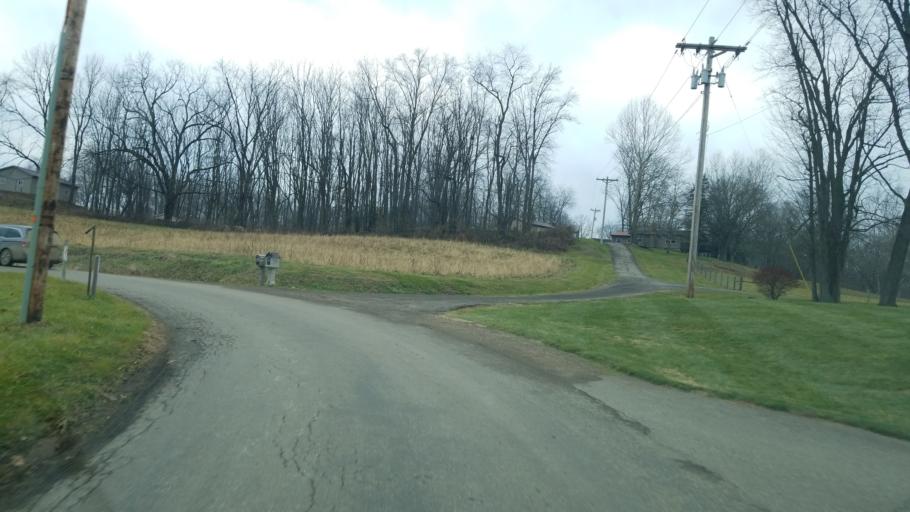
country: US
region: Ohio
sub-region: Holmes County
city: Millersburg
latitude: 40.6453
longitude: -81.9186
